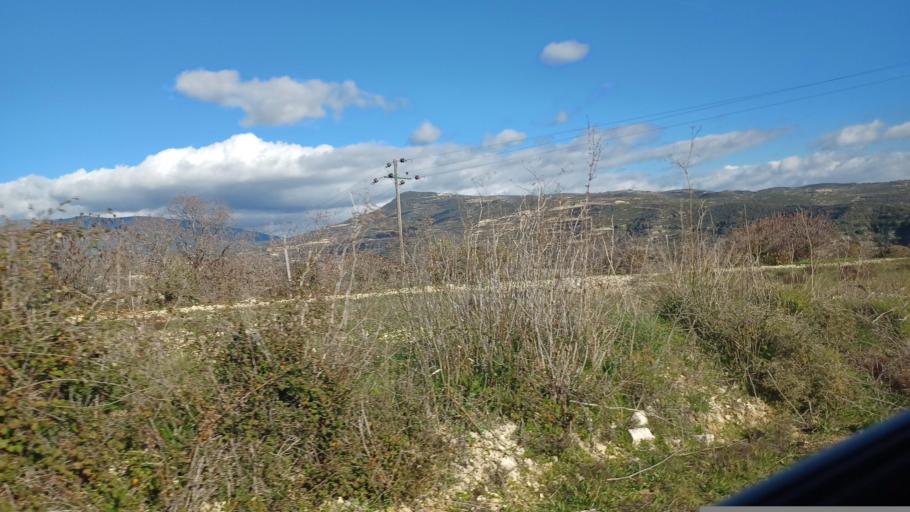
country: CY
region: Limassol
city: Pachna
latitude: 34.8388
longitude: 32.8060
